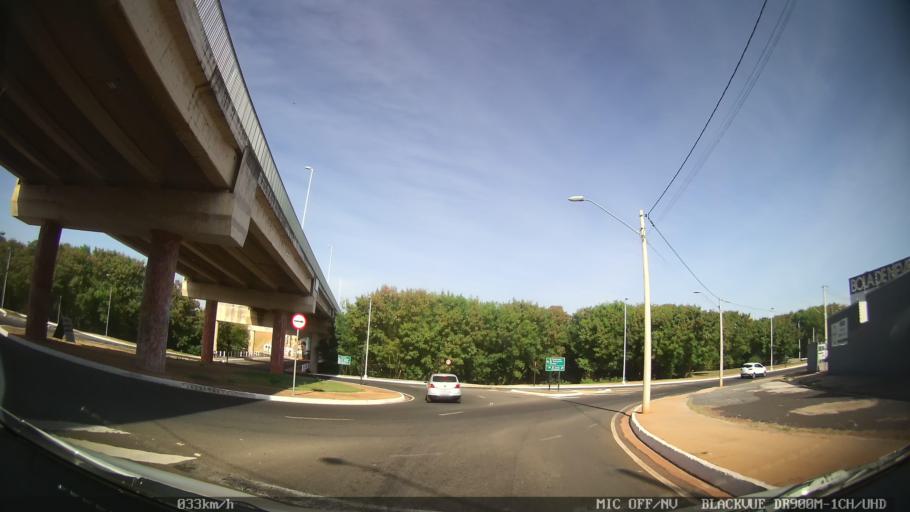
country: BR
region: Sao Paulo
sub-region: Sao Jose Do Rio Preto
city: Sao Jose do Rio Preto
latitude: -20.8017
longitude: -49.4079
